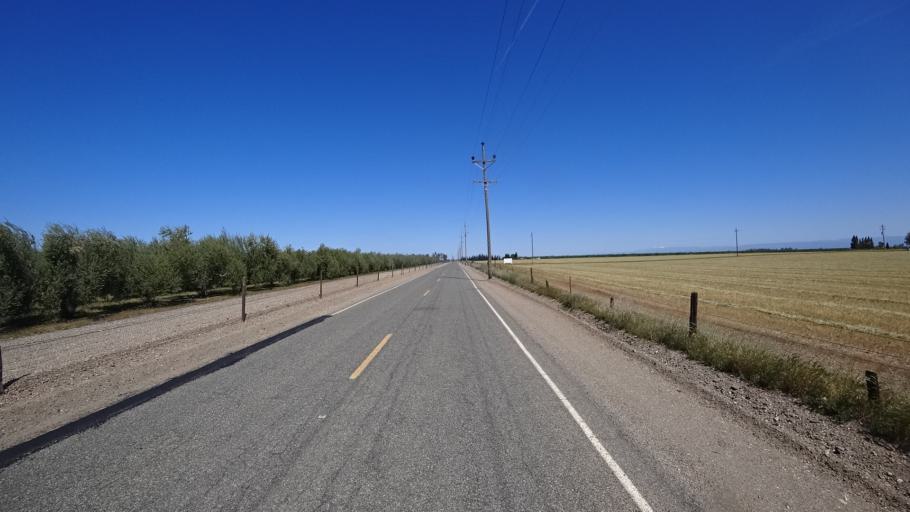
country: US
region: California
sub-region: Glenn County
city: Orland
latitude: 39.6611
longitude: -122.1784
